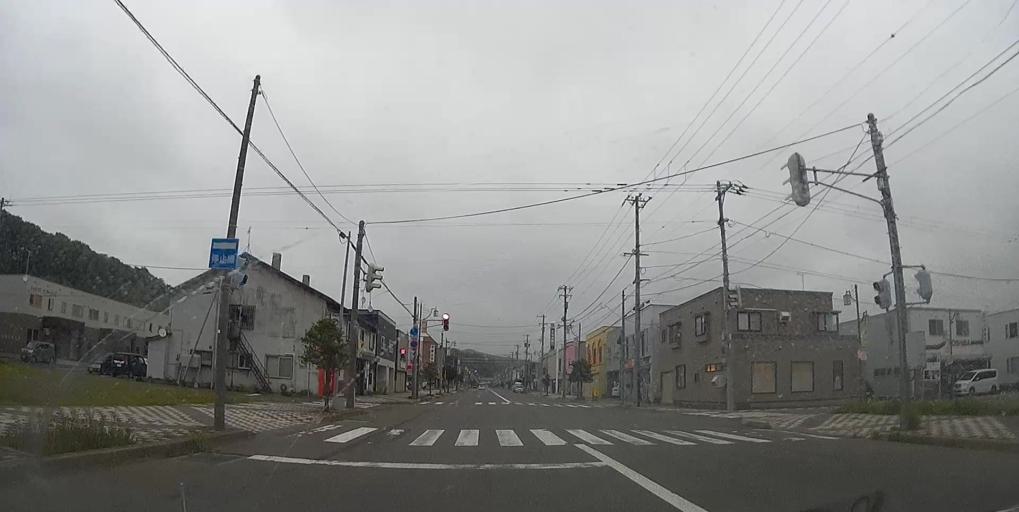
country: JP
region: Hokkaido
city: Iwanai
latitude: 42.4289
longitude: 140.0098
